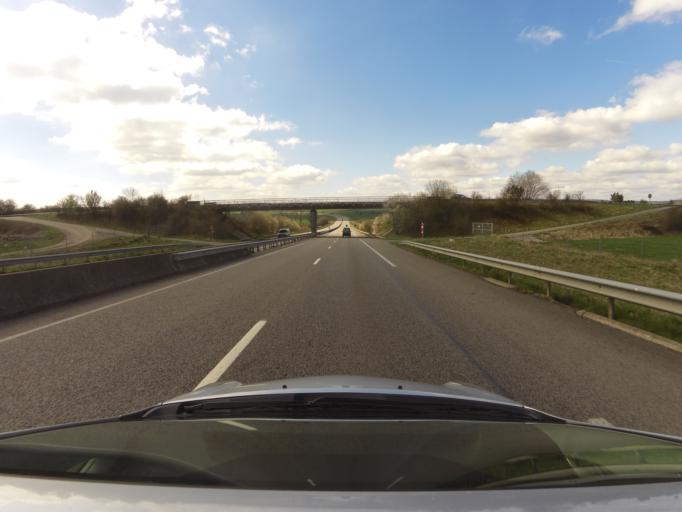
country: FR
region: Haute-Normandie
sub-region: Departement de la Seine-Maritime
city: Neufchatel-en-Bray
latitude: 49.7859
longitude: 1.4864
